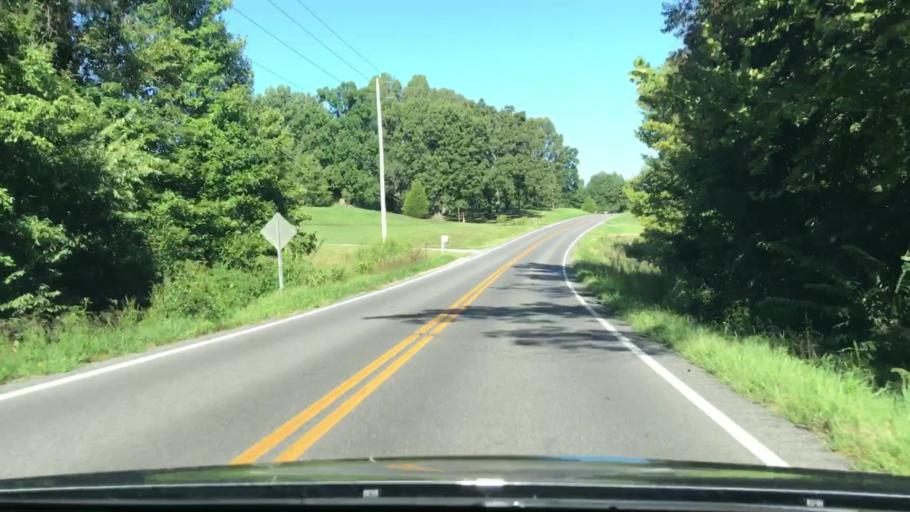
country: US
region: Kentucky
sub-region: Graves County
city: Mayfield
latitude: 36.7739
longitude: -88.5029
